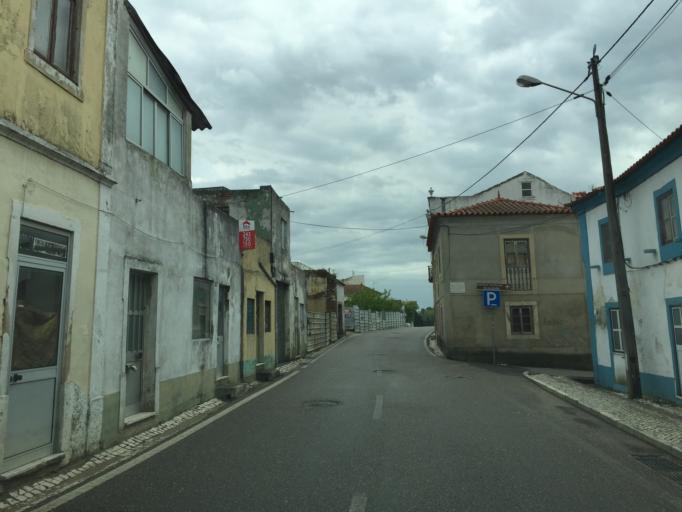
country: PT
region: Lisbon
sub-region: Azambuja
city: Aveiras de Cima
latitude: 39.1364
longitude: -8.8985
